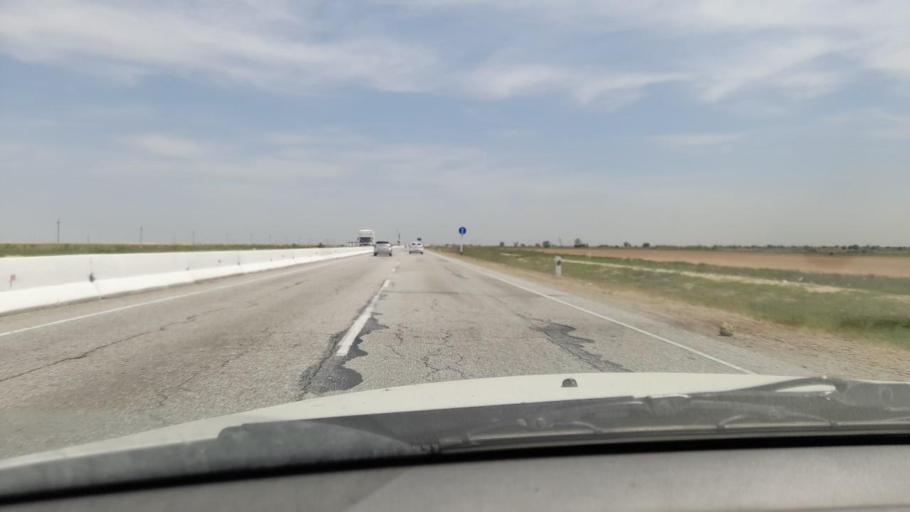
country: UZ
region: Navoiy
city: Qiziltepa
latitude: 40.0994
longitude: 64.9985
